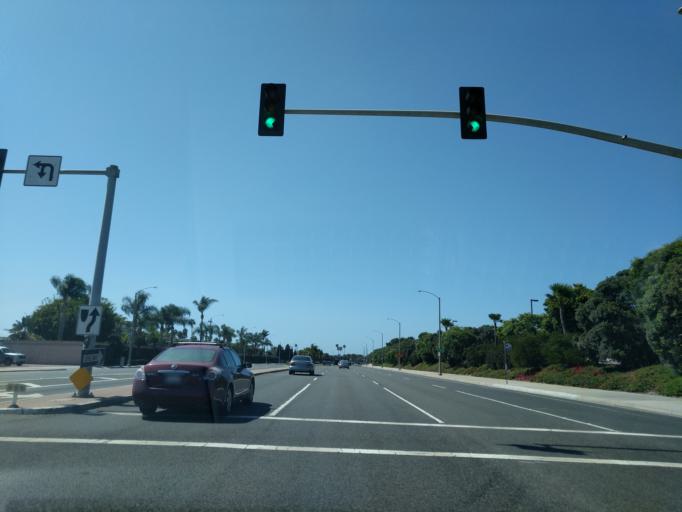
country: US
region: California
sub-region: Orange County
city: Newport Beach
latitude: 33.6217
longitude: -117.9333
